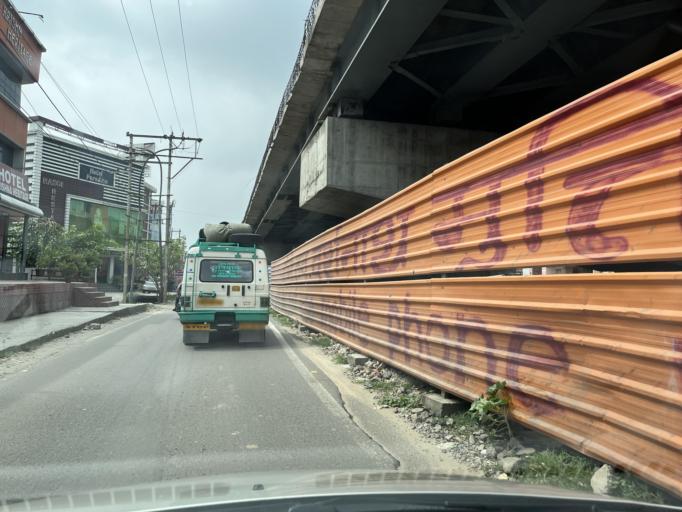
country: IN
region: Uttarakhand
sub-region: Haridwar
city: Haridwar
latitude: 29.9810
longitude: 78.1830
